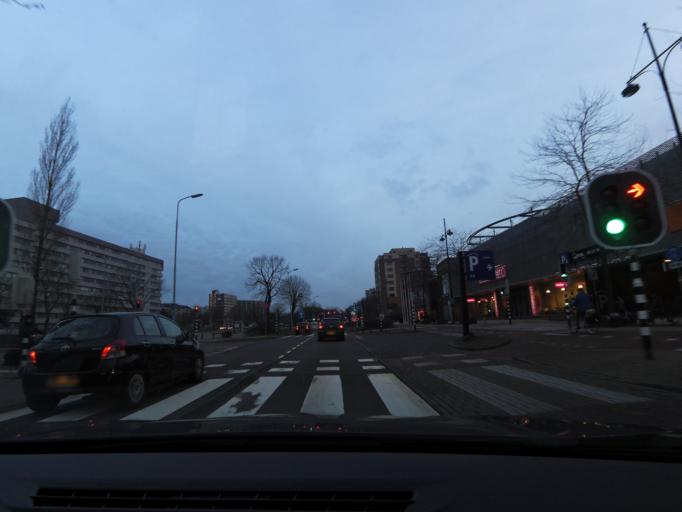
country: NL
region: South Holland
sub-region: Gemeente Rijswijk
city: Rijswijk
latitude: 52.0370
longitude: 4.3135
